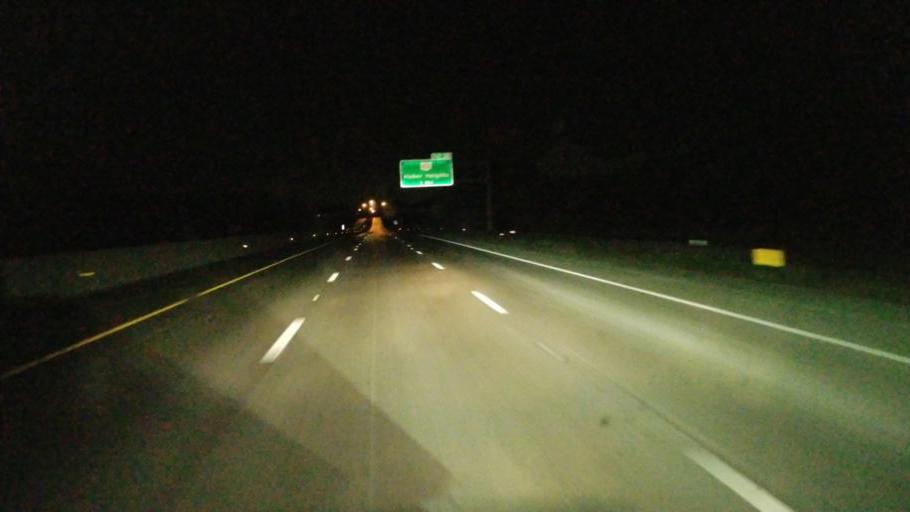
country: US
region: Ohio
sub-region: Clark County
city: Park Layne
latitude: 39.8665
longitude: -84.0759
